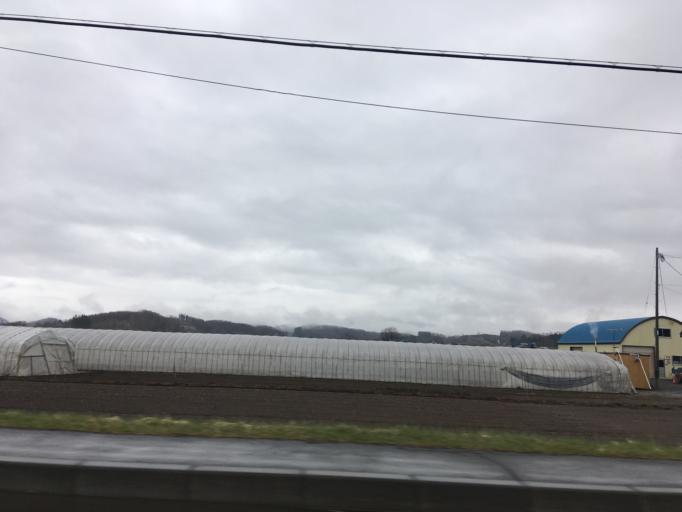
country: JP
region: Hokkaido
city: Nayoro
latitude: 44.1149
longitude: 142.4803
